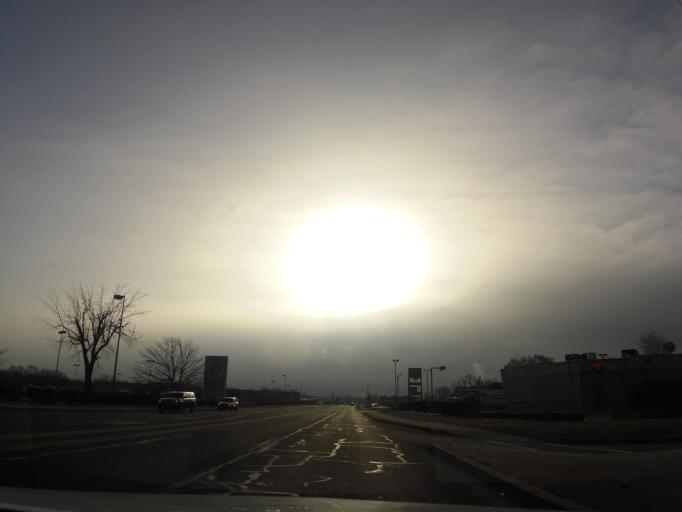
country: US
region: Indiana
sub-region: Bartholomew County
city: Columbus
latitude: 39.2204
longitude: -85.8881
